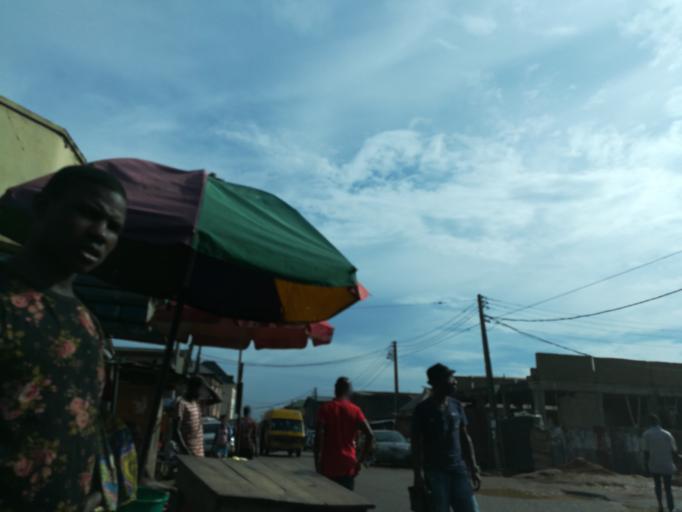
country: NG
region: Lagos
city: Oshodi
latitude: 6.5609
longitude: 3.3478
